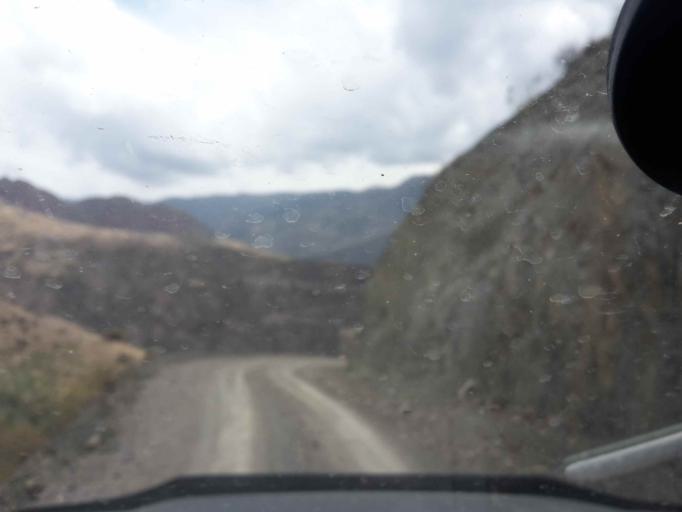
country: BO
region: Cochabamba
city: Colchani
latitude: -17.5151
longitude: -66.6059
